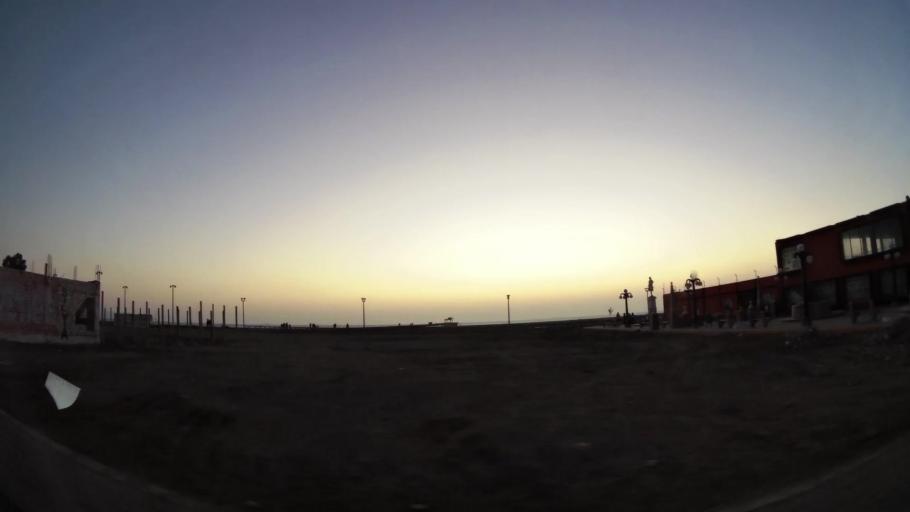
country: PE
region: Ica
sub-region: Provincia de Pisco
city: Pisco
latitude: -13.7095
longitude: -76.2181
